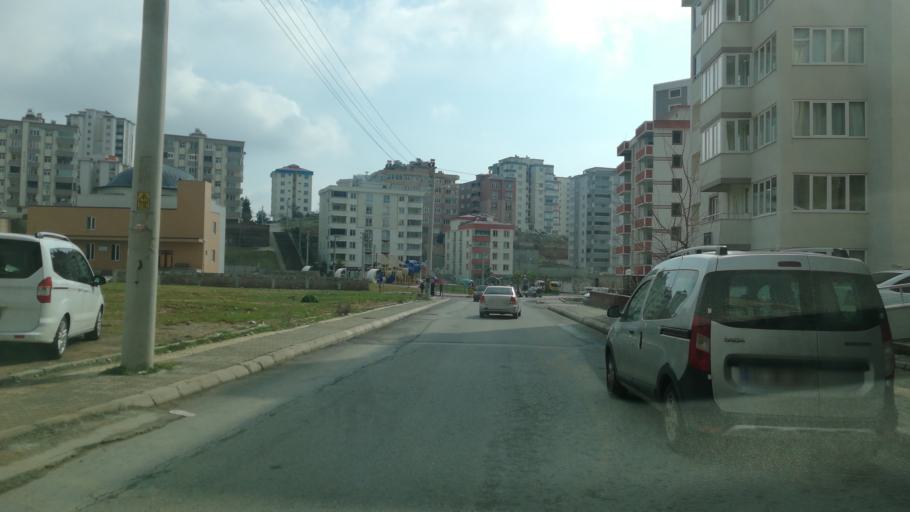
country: TR
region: Kahramanmaras
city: Kahramanmaras
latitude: 37.5828
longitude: 36.8982
